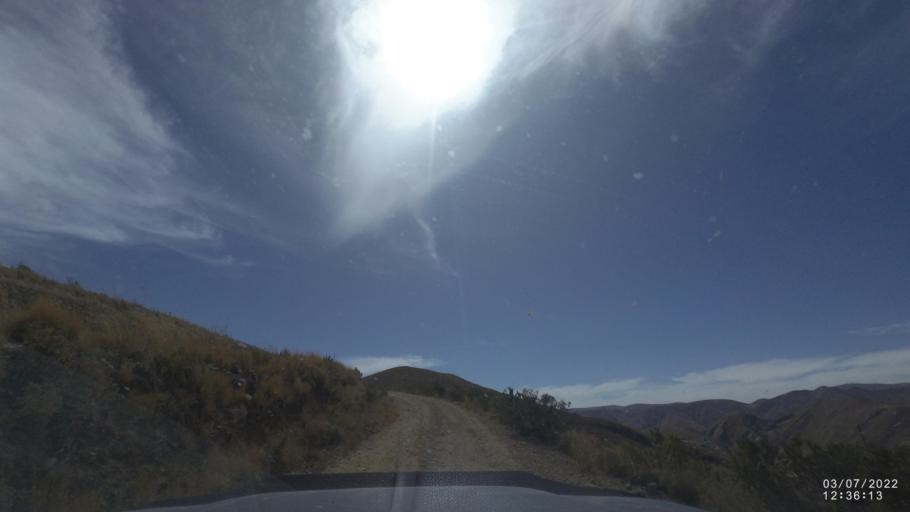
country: BO
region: Cochabamba
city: Irpa Irpa
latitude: -17.8026
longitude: -66.6120
